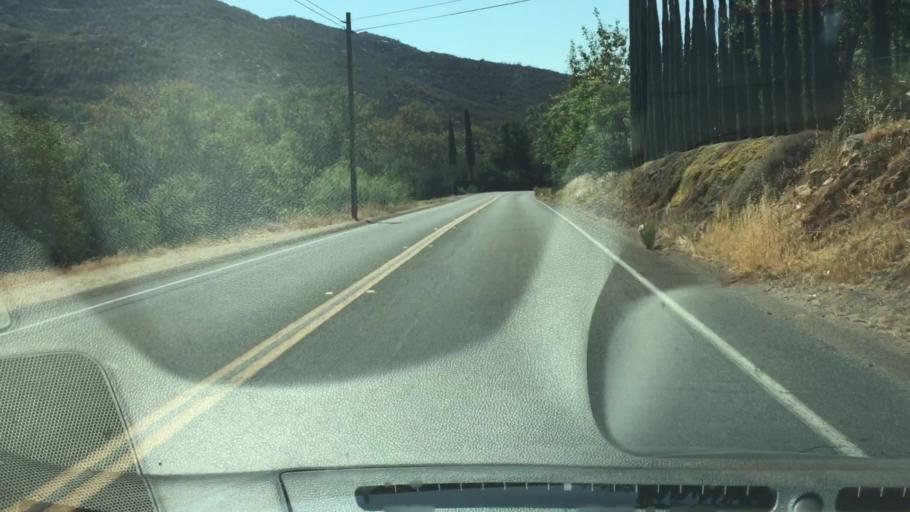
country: US
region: California
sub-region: San Diego County
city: Jamul
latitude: 32.7346
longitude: -116.8891
